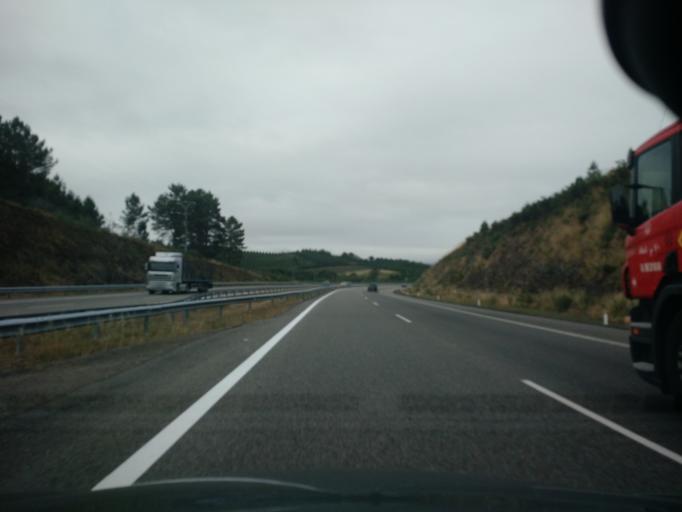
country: ES
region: Galicia
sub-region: Provincia da Coruna
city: Oroso
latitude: 42.9445
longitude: -8.4610
